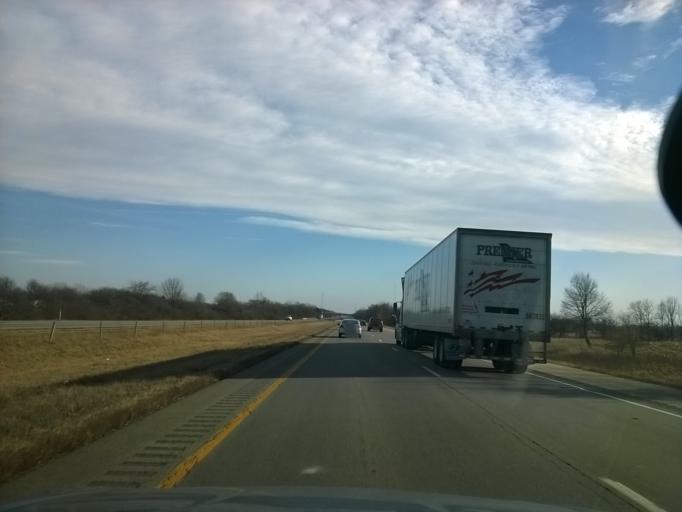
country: US
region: Indiana
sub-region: Johnson County
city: Franklin
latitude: 39.4487
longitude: -85.9939
